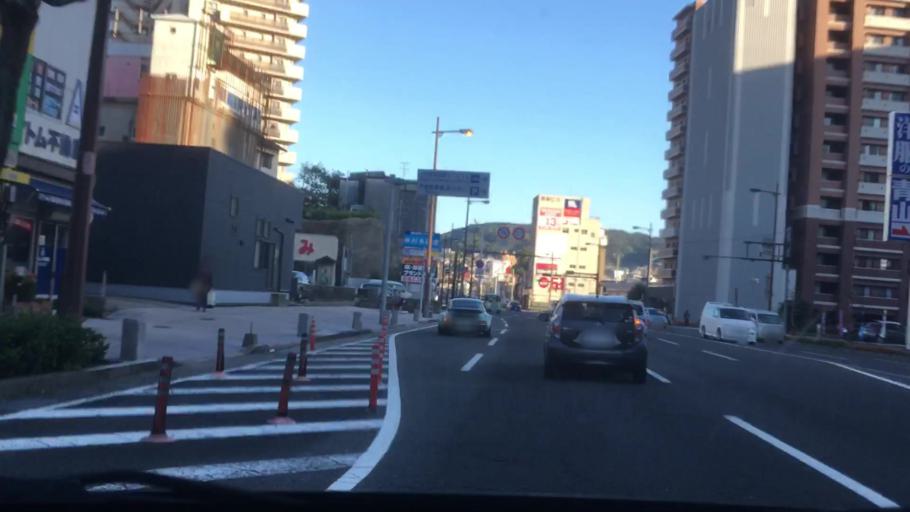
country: JP
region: Nagasaki
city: Sasebo
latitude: 33.1632
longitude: 129.7282
